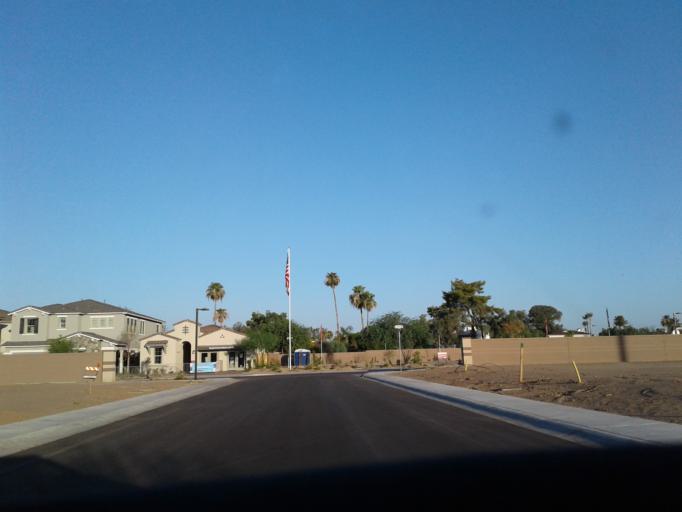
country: US
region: Arizona
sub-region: Maricopa County
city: Glendale
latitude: 33.6344
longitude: -112.0773
